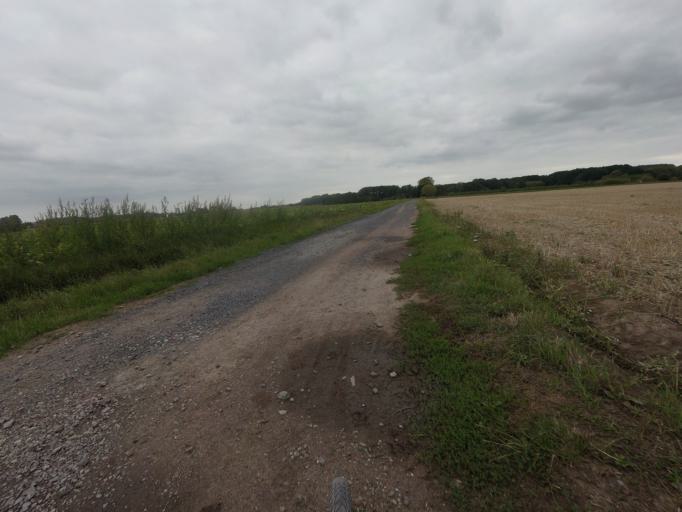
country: BE
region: Flanders
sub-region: Provincie Vlaams-Brabant
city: Herent
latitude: 50.9110
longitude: 4.6520
